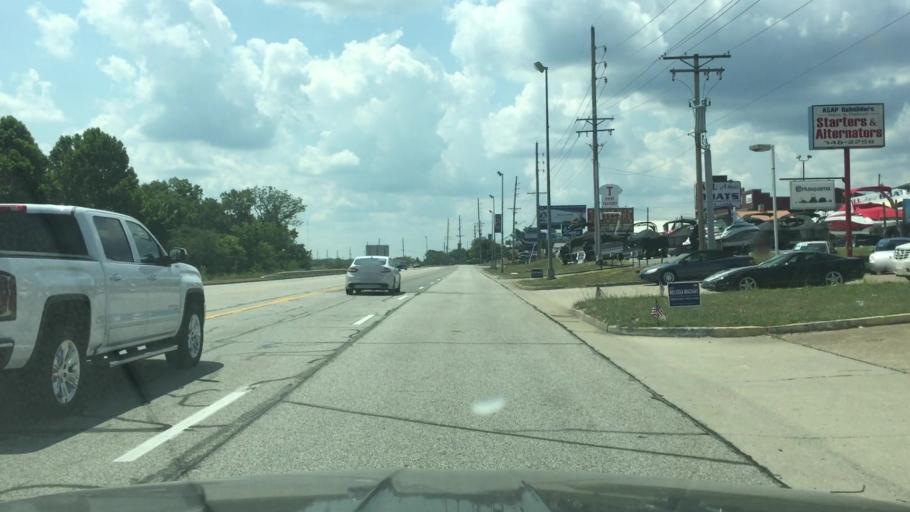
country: US
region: Missouri
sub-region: Miller County
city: Lake Ozark
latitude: 38.1689
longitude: -92.6114
